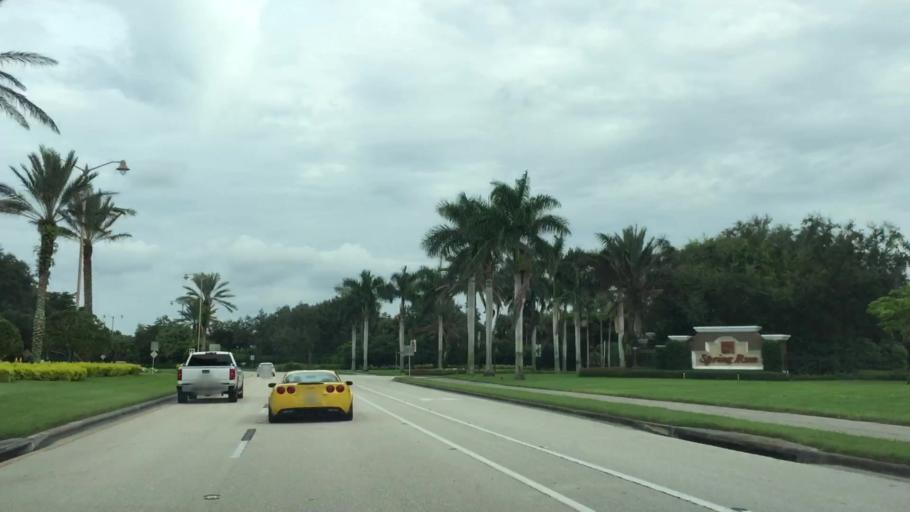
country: US
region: Florida
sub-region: Lee County
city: Estero
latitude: 26.3962
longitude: -81.7956
